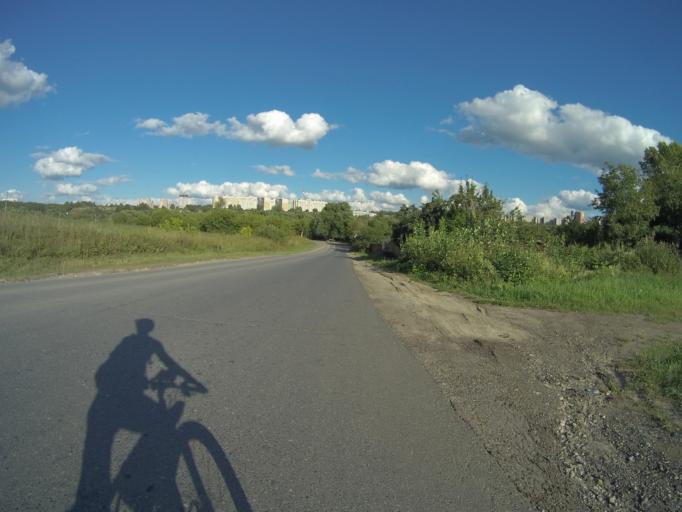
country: RU
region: Vladimir
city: Vladimir
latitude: 56.1617
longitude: 40.3586
